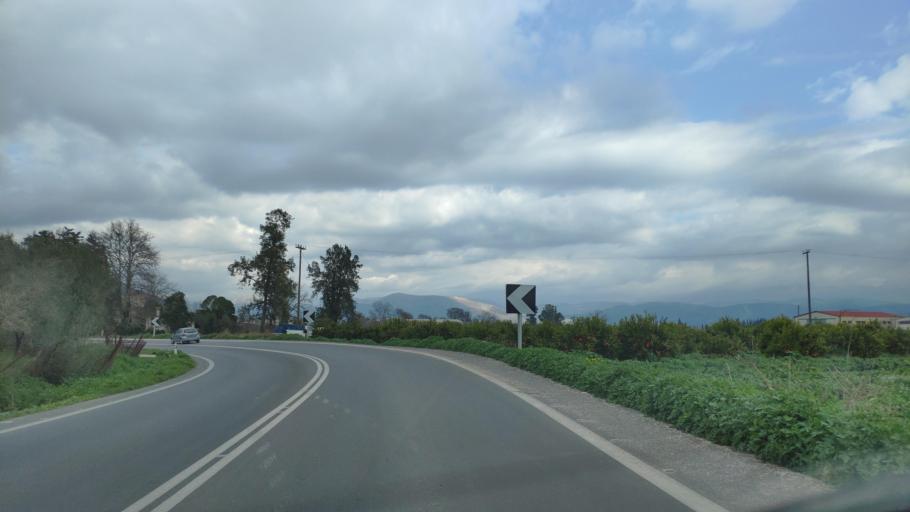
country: GR
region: Peloponnese
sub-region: Nomos Argolidos
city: Nea Kios
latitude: 37.6035
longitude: 22.7088
